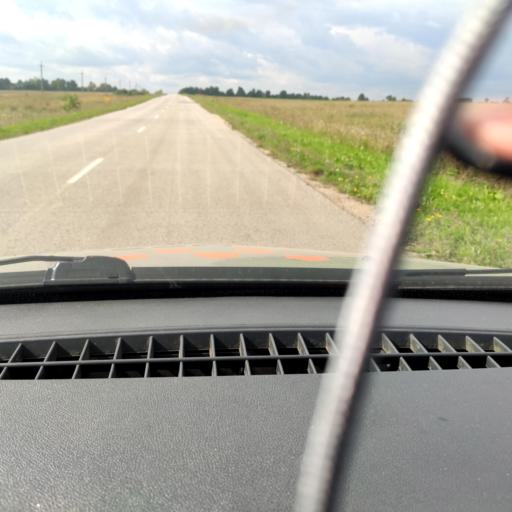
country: RU
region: Bashkortostan
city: Iglino
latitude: 54.7590
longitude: 56.5696
